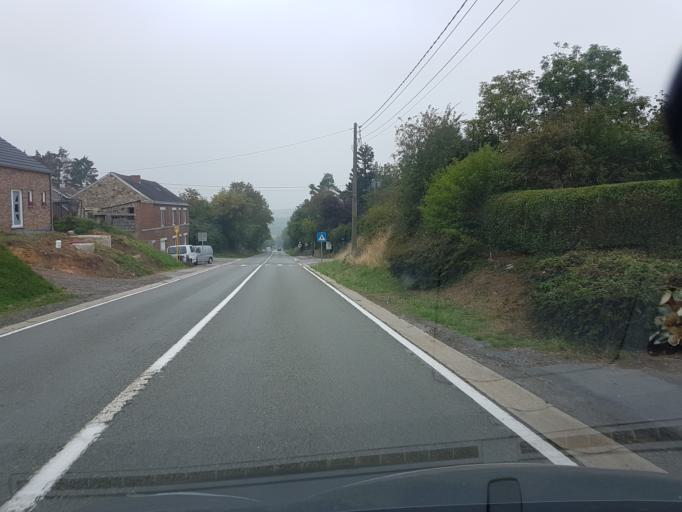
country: BE
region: Wallonia
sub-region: Province de Namur
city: Ohey
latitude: 50.4562
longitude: 5.1089
